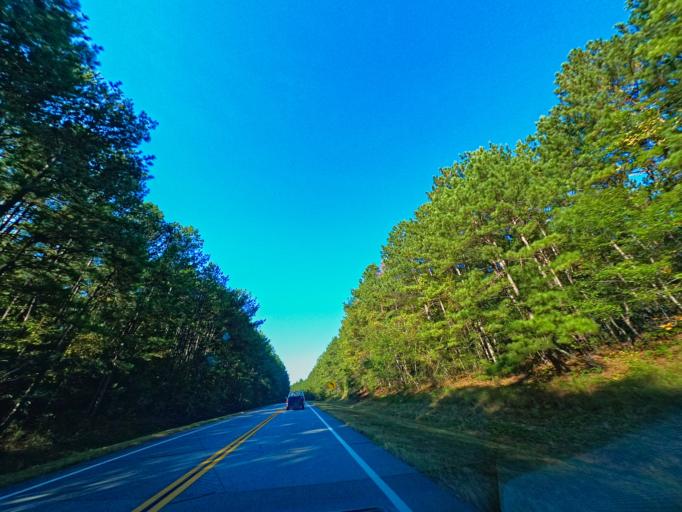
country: US
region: Georgia
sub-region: Coweta County
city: Newnan
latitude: 33.3910
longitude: -84.8442
